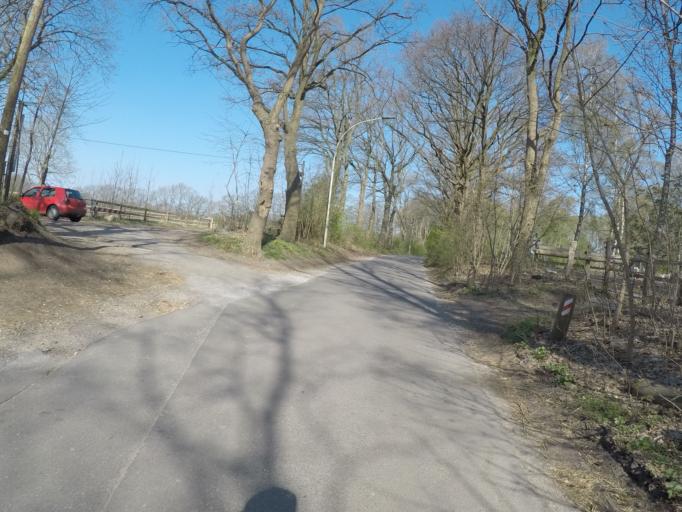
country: DE
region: Schleswig-Holstein
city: Rellingen
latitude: 53.5984
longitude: 9.8117
